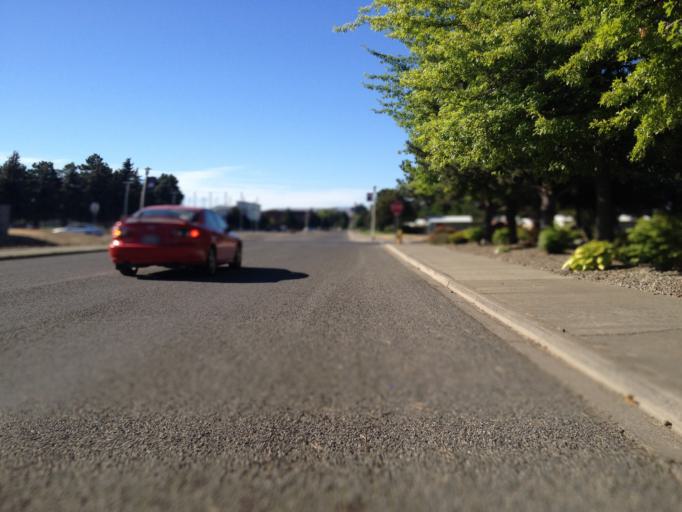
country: US
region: Washington
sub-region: Kittitas County
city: Ellensburg
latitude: 47.0109
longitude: -120.5398
